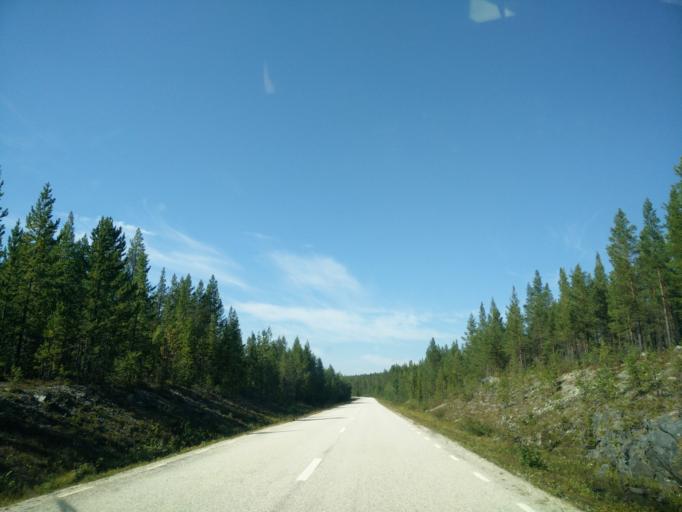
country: SE
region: Jaemtland
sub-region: Are Kommun
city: Jarpen
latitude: 62.8194
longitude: 13.5074
